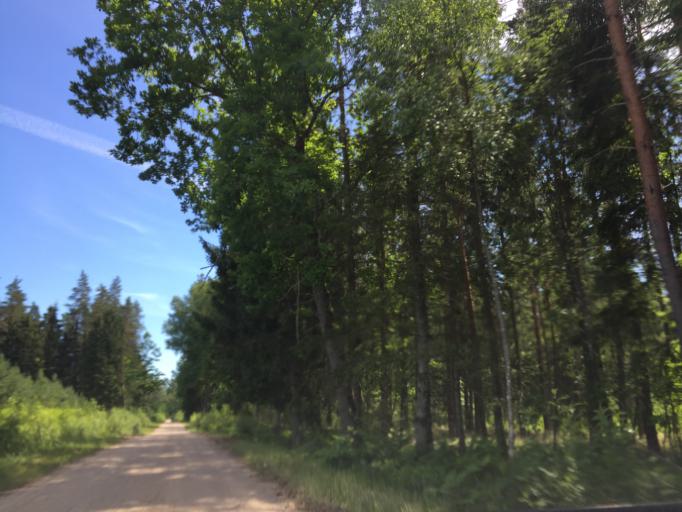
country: LV
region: Kuldigas Rajons
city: Kuldiga
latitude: 57.1218
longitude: 21.8692
